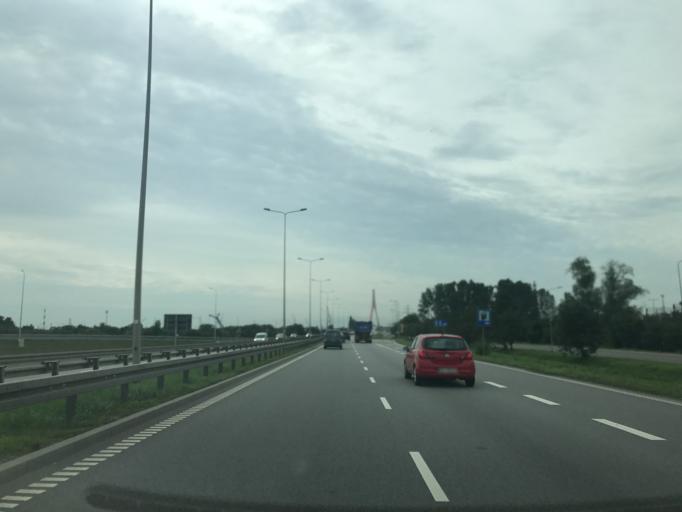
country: PL
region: Pomeranian Voivodeship
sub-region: Gdansk
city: Gdansk
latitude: 54.3667
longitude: 18.6878
